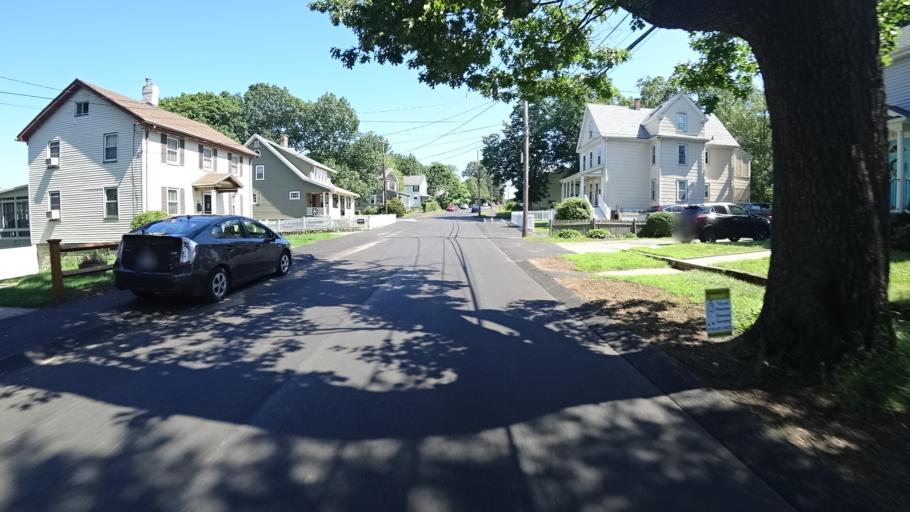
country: US
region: Massachusetts
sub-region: Norfolk County
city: Dedham
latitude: 42.2399
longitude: -71.1506
